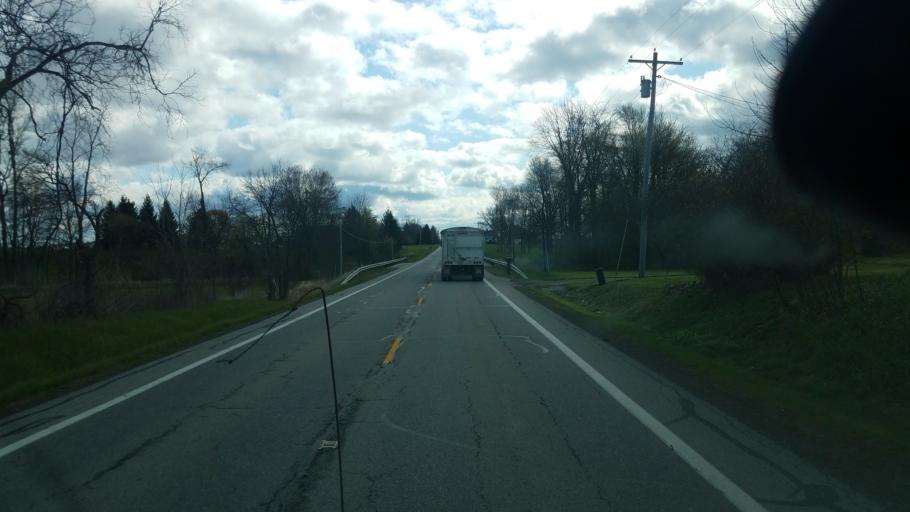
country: US
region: Ohio
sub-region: Morrow County
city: Cardington
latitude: 40.5854
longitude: -82.9736
